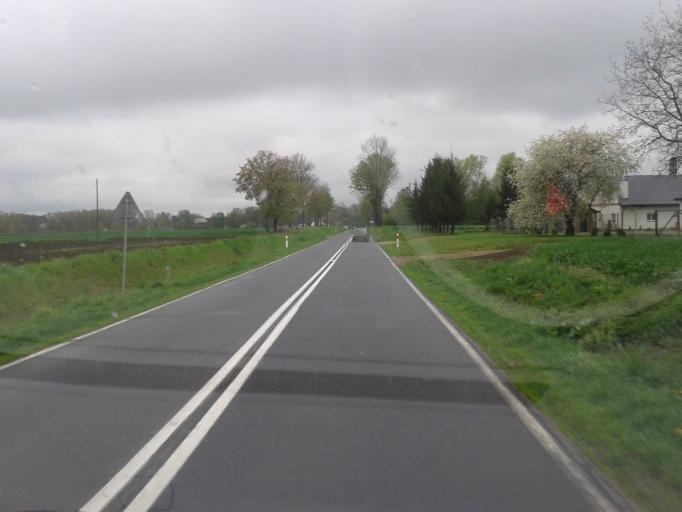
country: PL
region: Lublin Voivodeship
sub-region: Powiat hrubieszowski
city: Mircze
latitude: 50.5628
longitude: 23.9375
